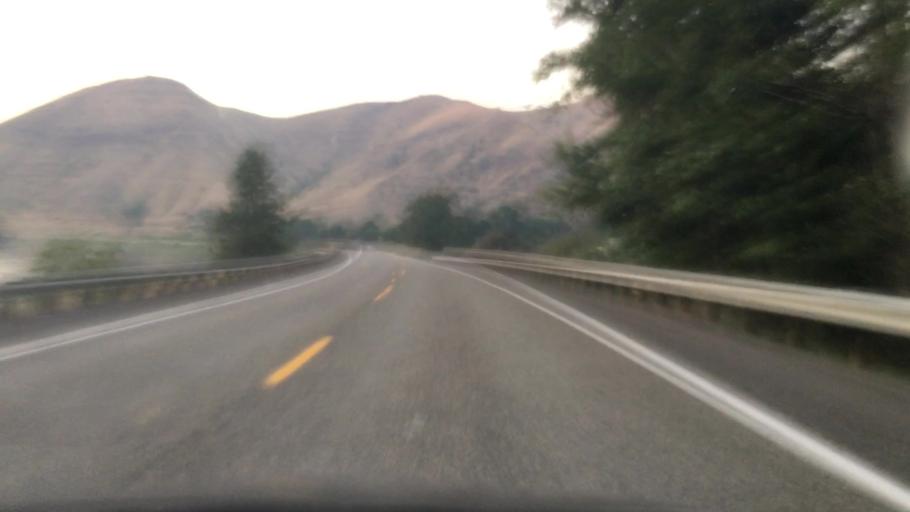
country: US
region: Idaho
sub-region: Idaho County
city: Grangeville
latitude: 45.6334
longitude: -116.2838
